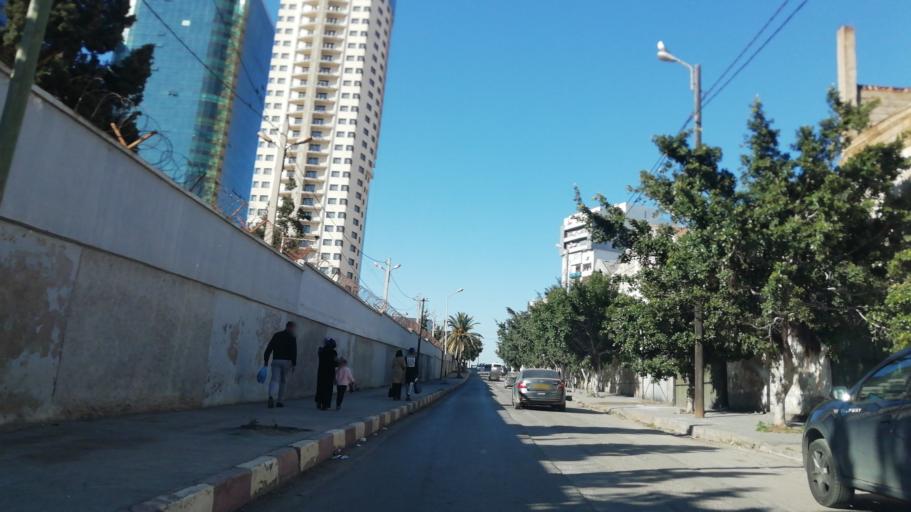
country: DZ
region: Oran
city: Oran
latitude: 35.7107
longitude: -0.6227
